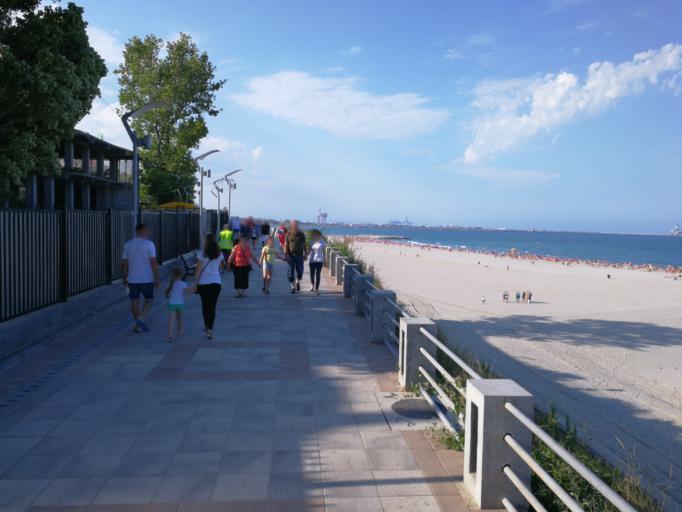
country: RO
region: Constanta
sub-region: Oras Eforie
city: Eforie Nord
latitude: 44.0635
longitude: 28.6395
